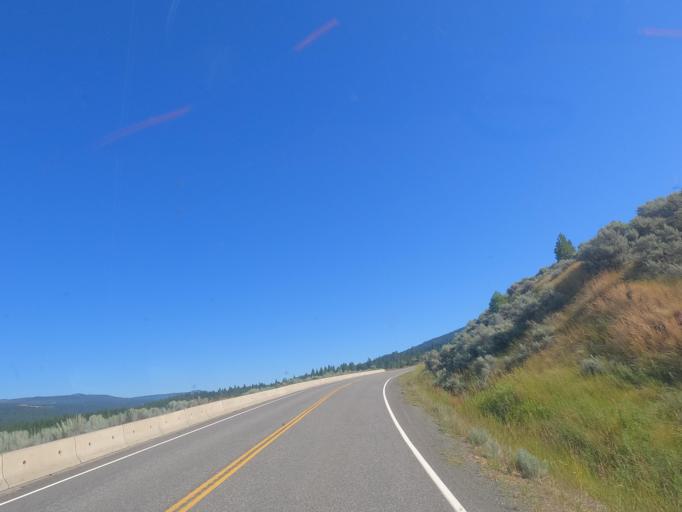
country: CA
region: British Columbia
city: Merritt
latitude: 50.1968
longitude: -120.8498
